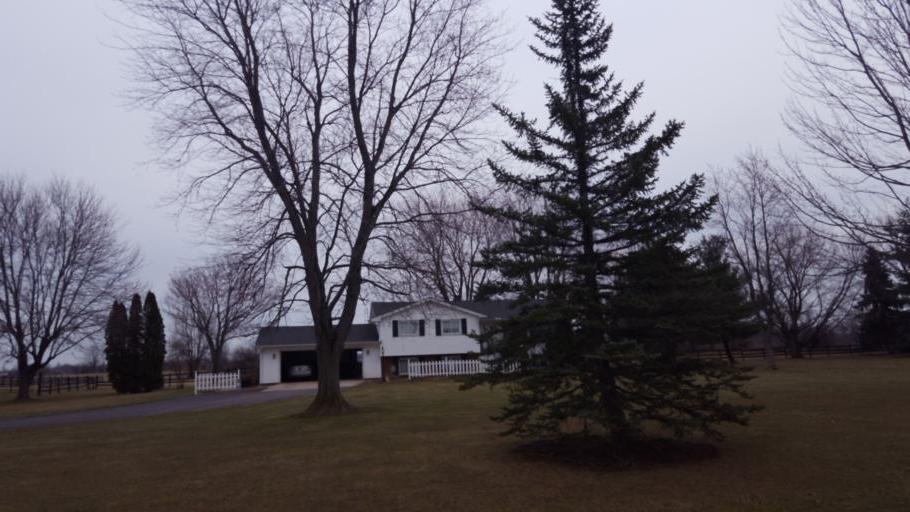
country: US
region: Ohio
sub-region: Crawford County
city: Crestline
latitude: 40.7823
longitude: -82.7263
